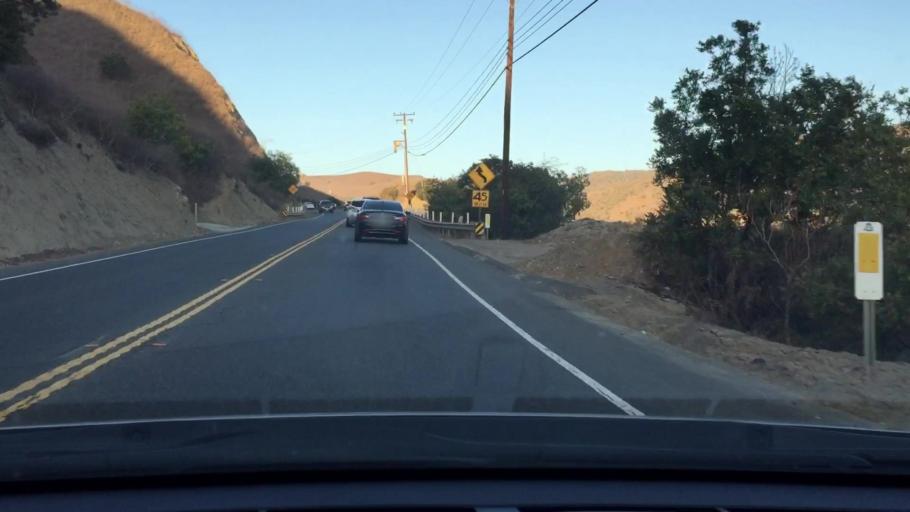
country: US
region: California
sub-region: Orange County
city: Yorba Linda
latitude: 33.9220
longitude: -117.8162
